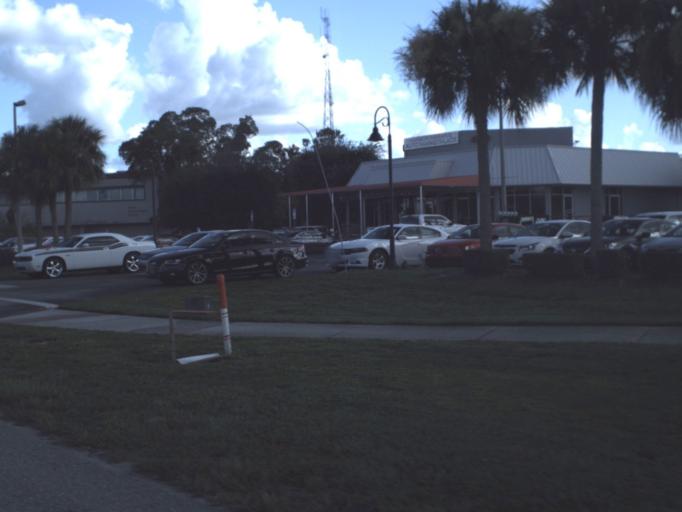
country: US
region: Florida
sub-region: Charlotte County
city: Charlotte Harbor
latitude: 26.9665
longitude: -82.0774
